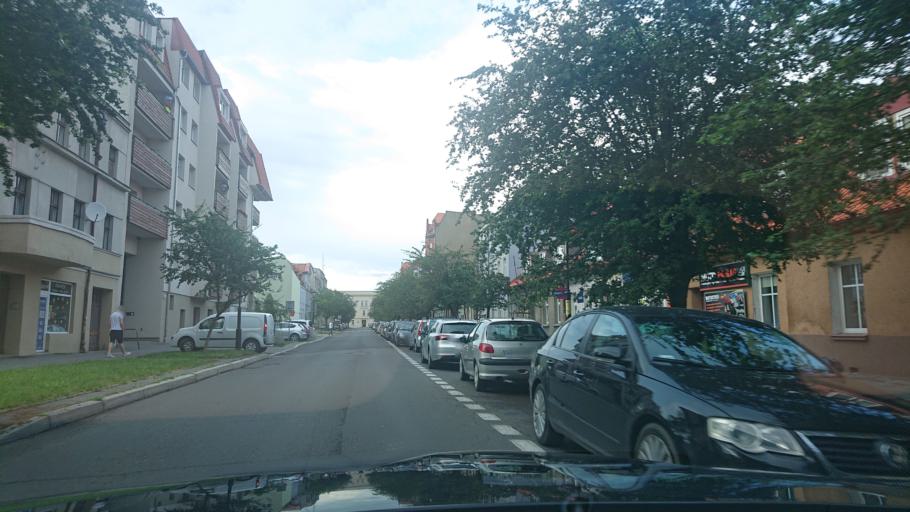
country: PL
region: Greater Poland Voivodeship
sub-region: Powiat gnieznienski
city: Gniezno
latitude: 52.5339
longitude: 17.6025
